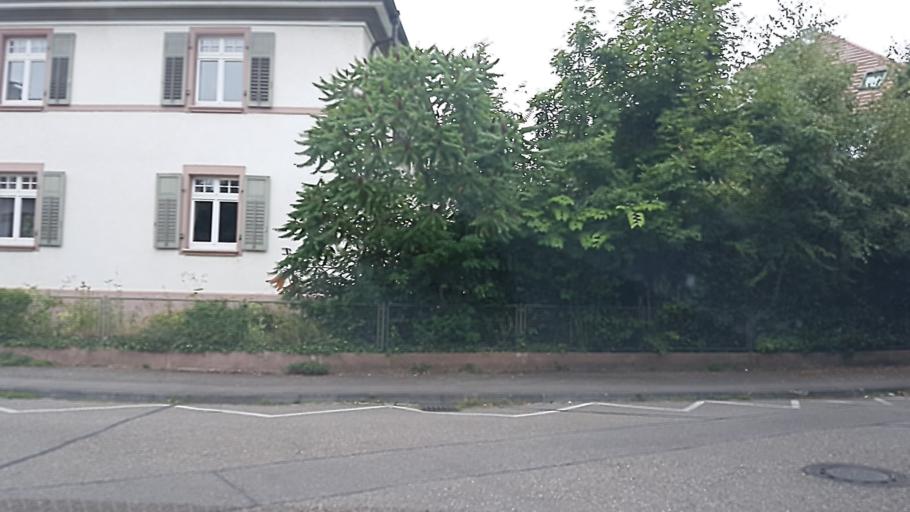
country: DE
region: Baden-Wuerttemberg
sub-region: Freiburg Region
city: Emmendingen
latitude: 48.1178
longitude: 7.8561
